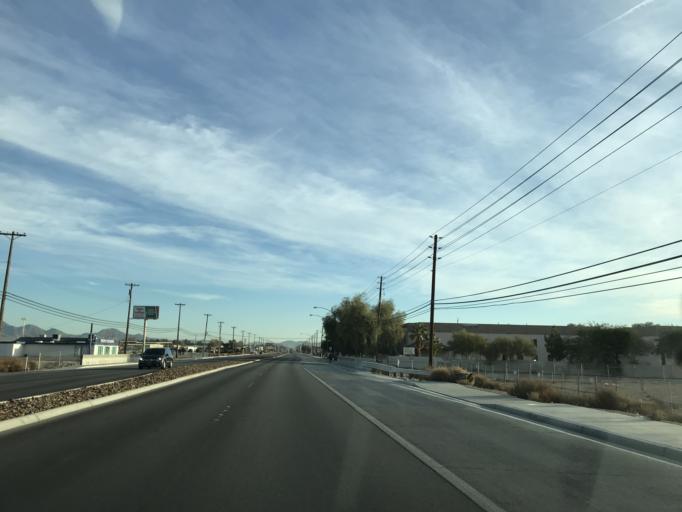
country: US
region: Nevada
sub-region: Clark County
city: Nellis Air Force Base
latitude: 36.2315
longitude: -115.0696
